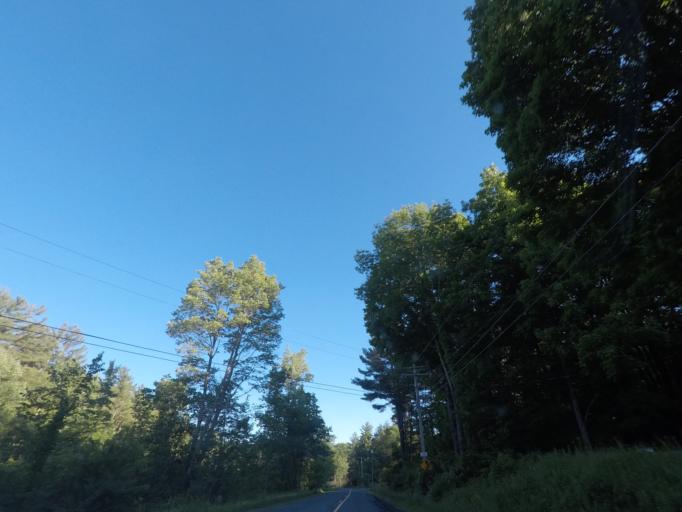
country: US
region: New York
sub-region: Rensselaer County
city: Averill Park
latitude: 42.5689
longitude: -73.5326
